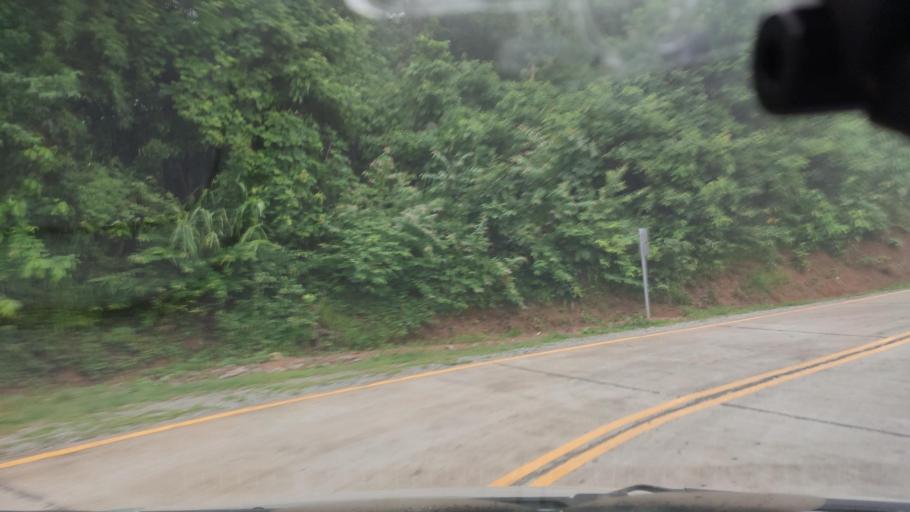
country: MM
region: Bago
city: Taungoo
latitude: 19.1189
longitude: 96.5020
